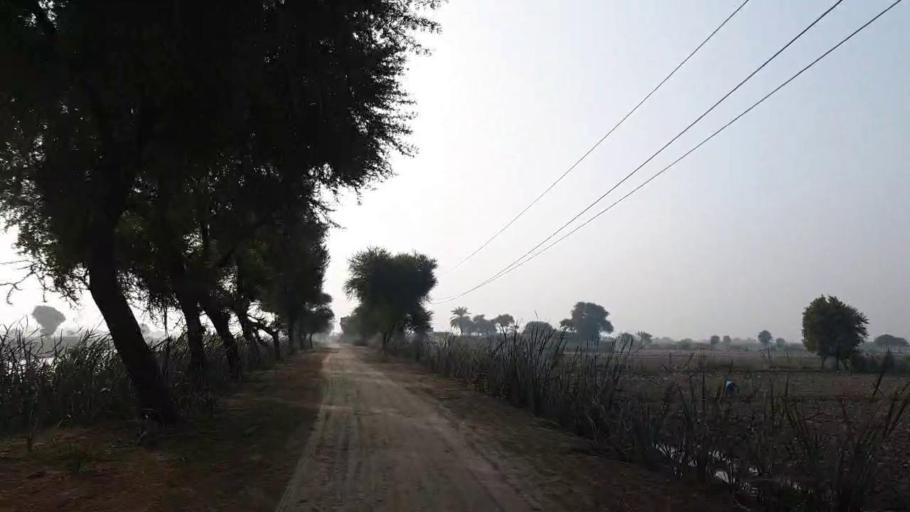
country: PK
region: Sindh
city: Tando Muhammad Khan
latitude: 25.1089
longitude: 68.5701
